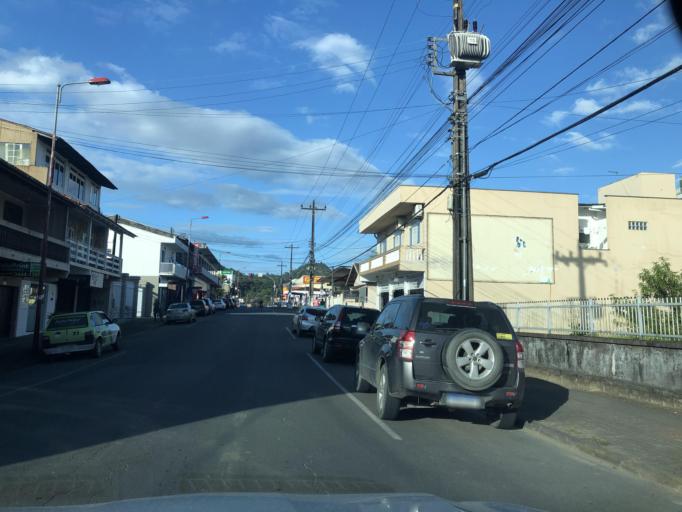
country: BR
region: Santa Catarina
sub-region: Sao Francisco Do Sul
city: Sao Francisco do Sul
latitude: -26.2502
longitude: -48.6362
